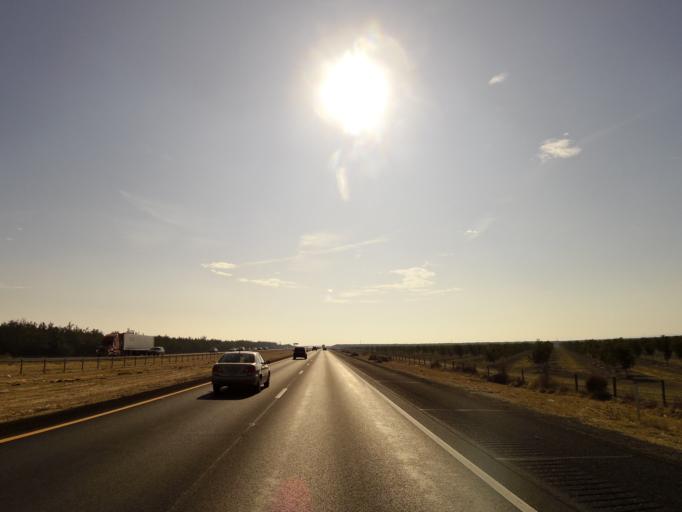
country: US
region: California
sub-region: Fresno County
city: Huron
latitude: 36.2160
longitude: -120.2201
